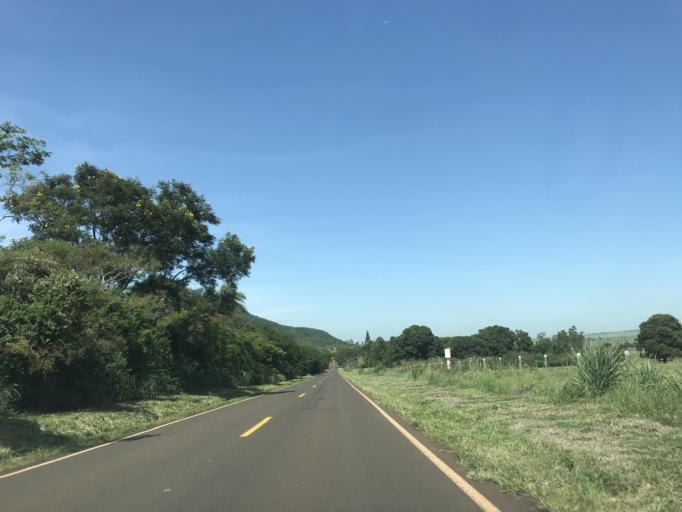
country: BR
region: Parana
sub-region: Terra Rica
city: Terra Rica
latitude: -22.7648
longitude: -52.6388
